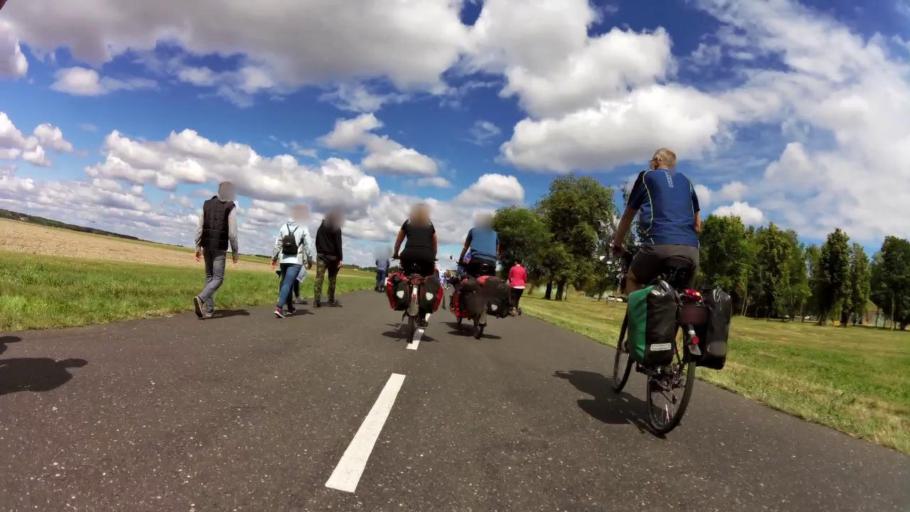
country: PL
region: West Pomeranian Voivodeship
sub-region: Powiat swidwinski
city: Swidwin
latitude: 53.7863
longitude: 15.8515
